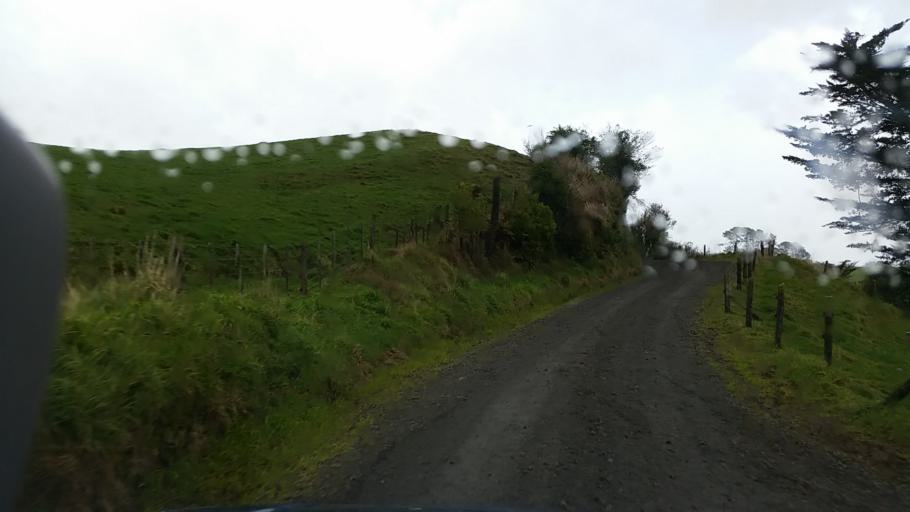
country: NZ
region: Taranaki
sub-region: South Taranaki District
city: Eltham
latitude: -39.2807
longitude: 174.3357
